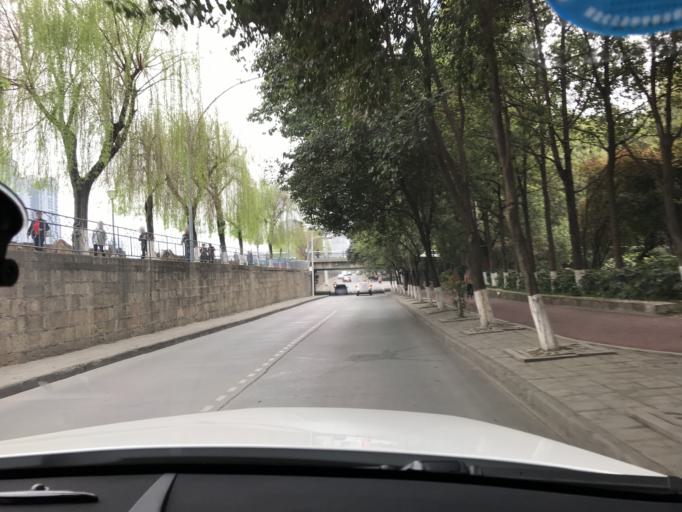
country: CN
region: Sichuan
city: Mianyang
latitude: 31.4540
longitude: 104.7470
